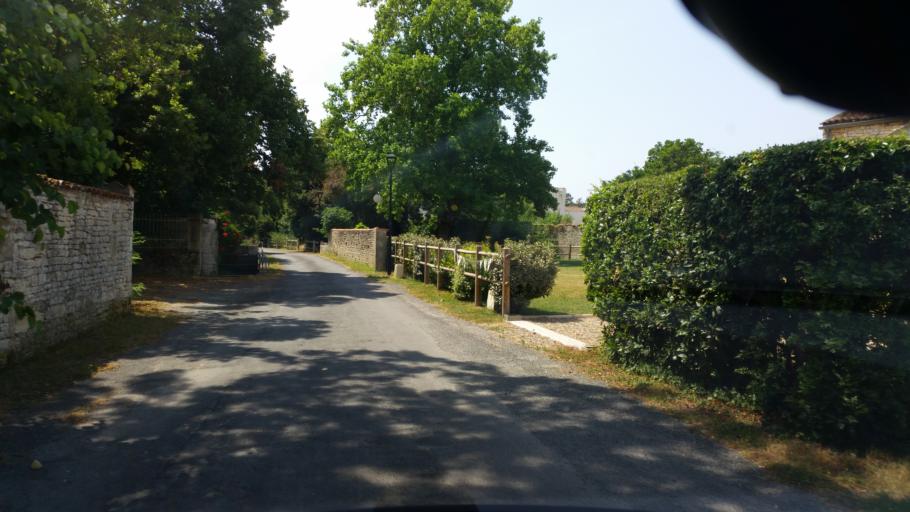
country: FR
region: Poitou-Charentes
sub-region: Departement de la Charente-Maritime
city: Saint-Jean-de-Liversay
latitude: 46.2164
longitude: -0.8858
